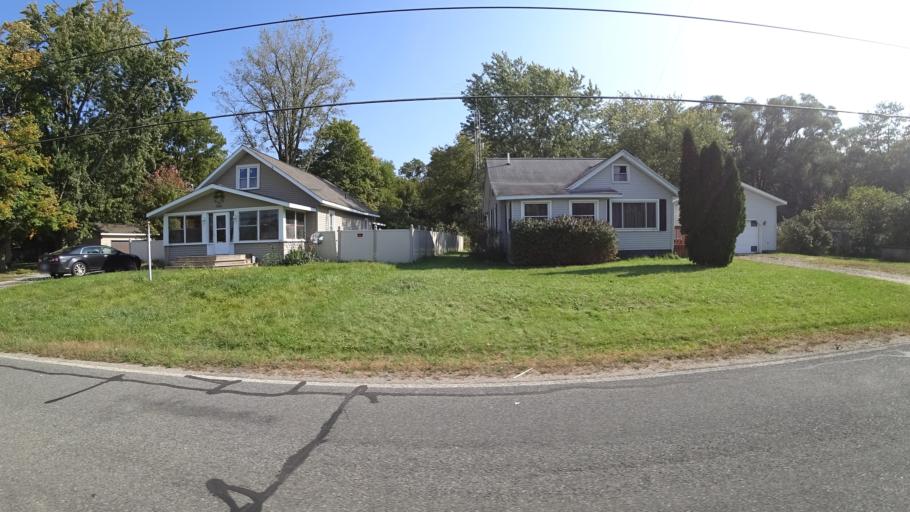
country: US
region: Michigan
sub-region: Saint Joseph County
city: Three Rivers
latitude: 41.9288
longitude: -85.6366
